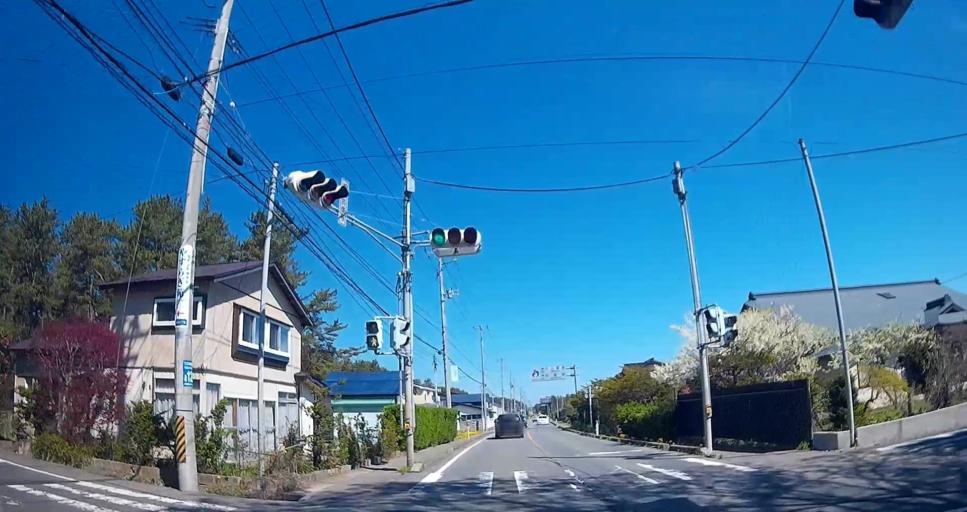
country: JP
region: Aomori
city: Misawa
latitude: 40.7356
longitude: 141.4110
